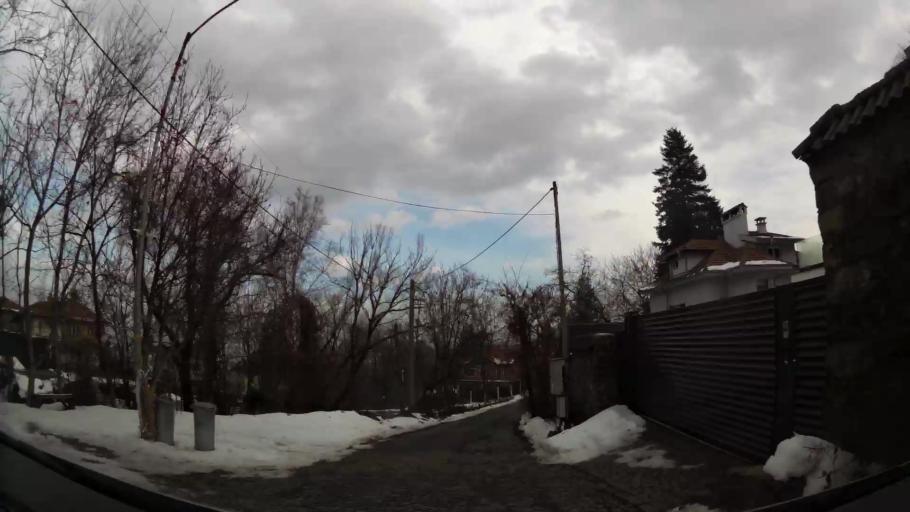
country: BG
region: Sofia-Capital
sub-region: Stolichna Obshtina
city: Sofia
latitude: 42.6449
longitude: 23.2634
